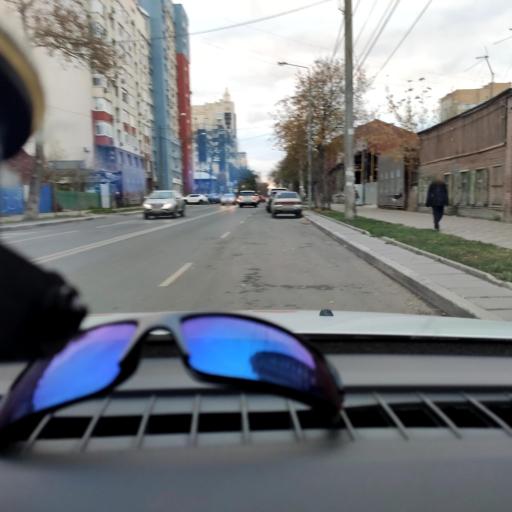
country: RU
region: Samara
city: Samara
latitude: 53.1953
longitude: 50.1123
